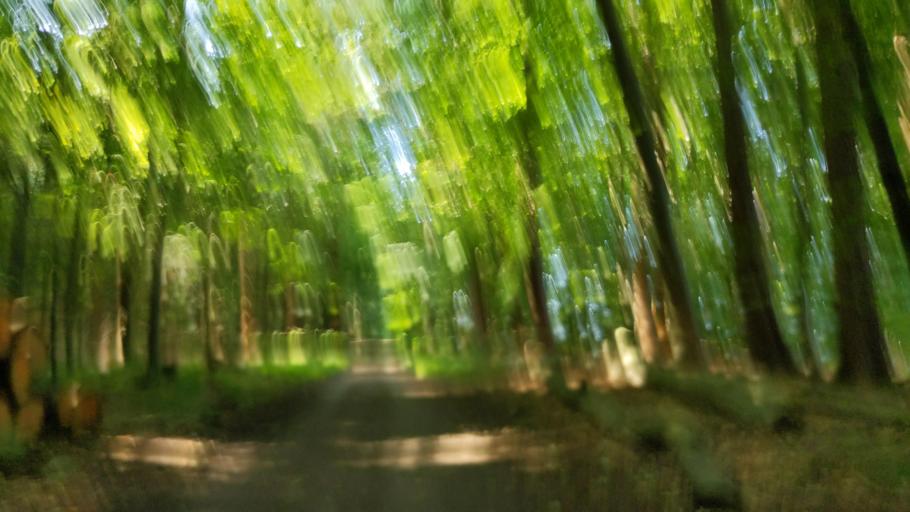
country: DE
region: Schleswig-Holstein
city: Bosdorf
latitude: 54.1614
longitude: 10.5108
